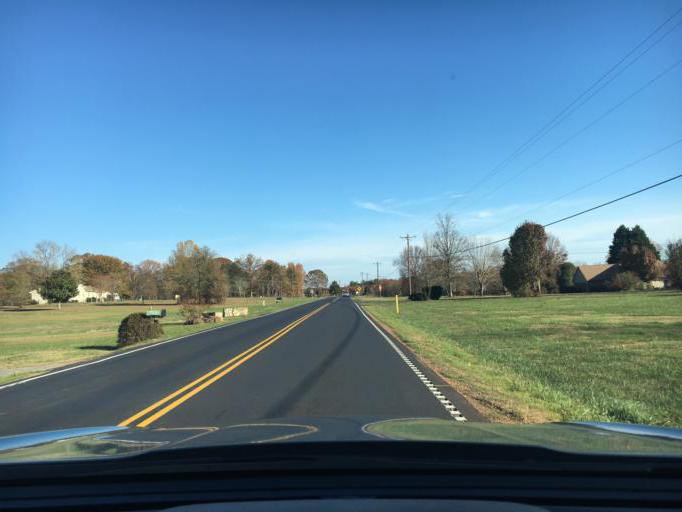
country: US
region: South Carolina
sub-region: Spartanburg County
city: Inman
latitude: 35.0246
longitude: -82.0887
